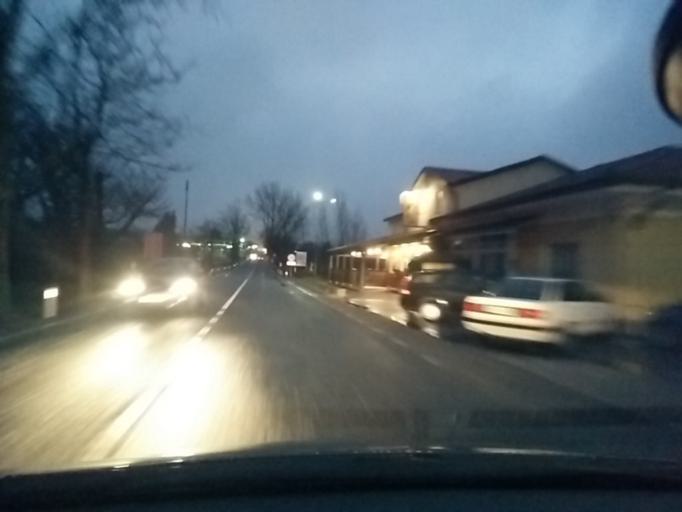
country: SI
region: Hrpelje-Kozina
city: Kozina
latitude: 45.6194
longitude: 13.9092
